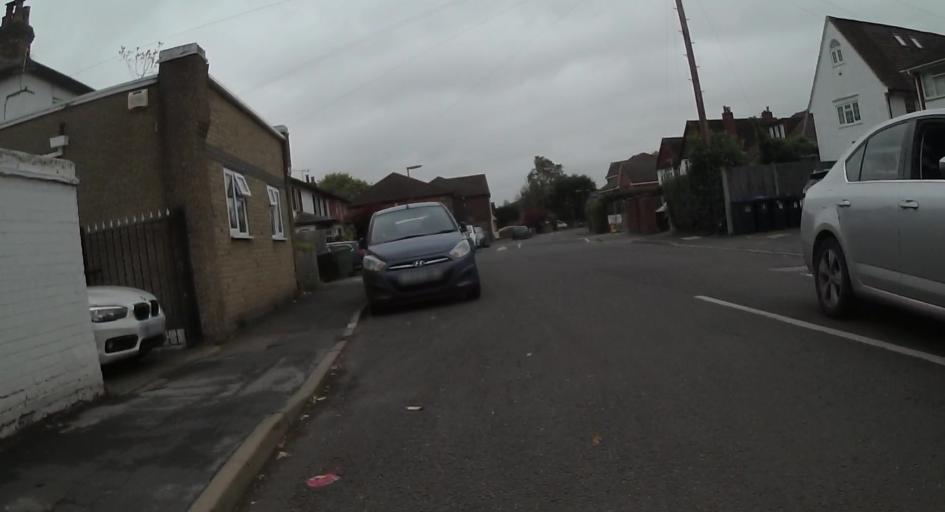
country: GB
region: England
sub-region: Surrey
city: Byfleet
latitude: 51.3441
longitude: -0.4812
